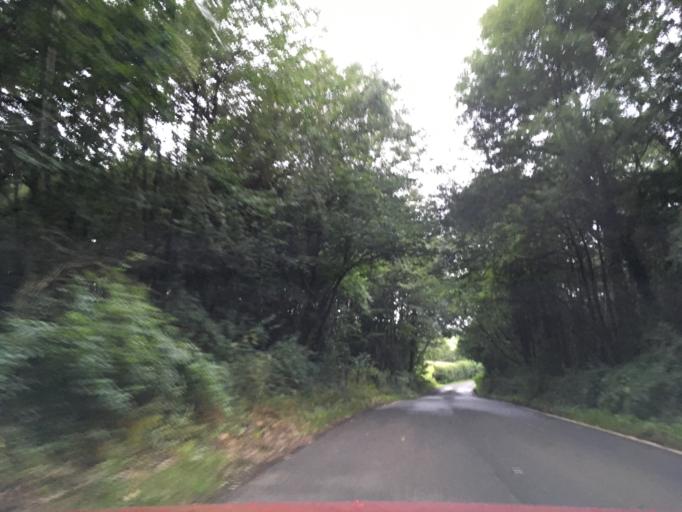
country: GB
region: Wales
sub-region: Monmouthshire
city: Llangwm
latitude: 51.6604
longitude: -2.8590
